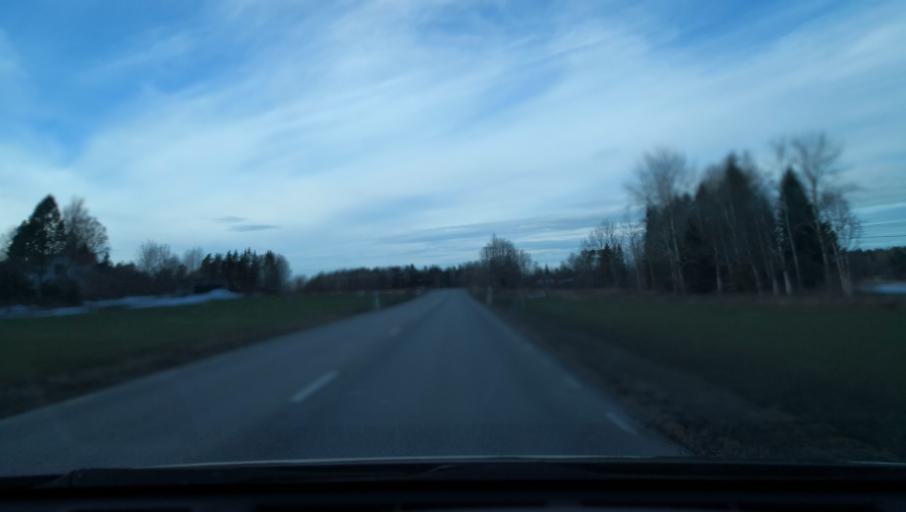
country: SE
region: Uppsala
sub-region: Osthammars Kommun
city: OEsthammar
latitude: 60.3050
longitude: 18.2729
